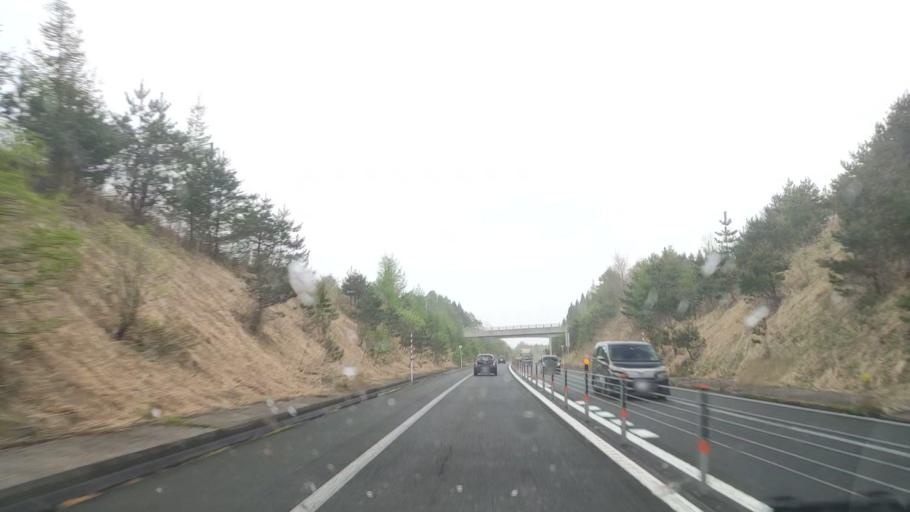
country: JP
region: Akita
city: Noshiromachi
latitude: 40.2029
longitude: 140.1563
